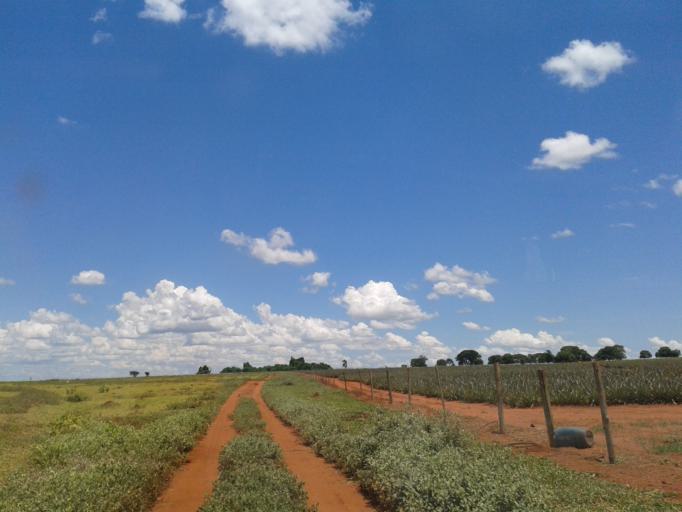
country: BR
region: Minas Gerais
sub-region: Centralina
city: Centralina
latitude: -18.7023
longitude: -49.1623
